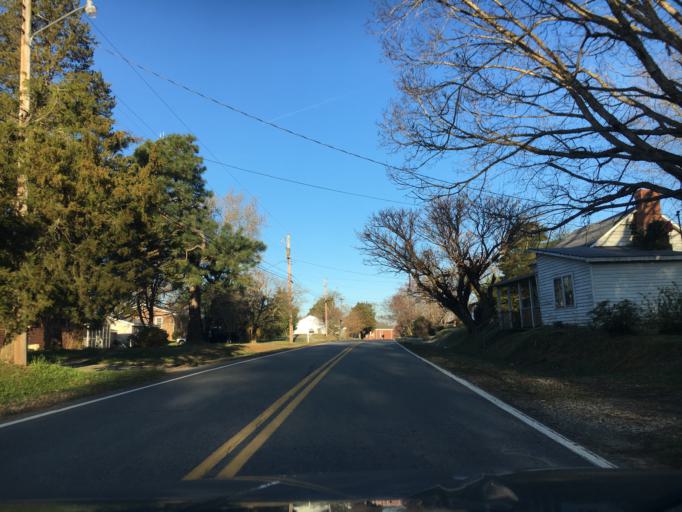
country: US
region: Virginia
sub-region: Halifax County
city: Halifax
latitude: 36.7687
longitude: -78.9203
